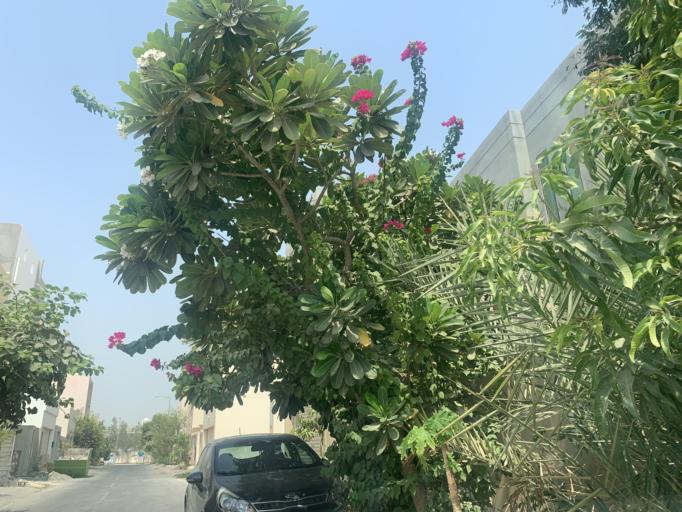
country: BH
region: Manama
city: Jidd Hafs
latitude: 26.2103
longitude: 50.5046
